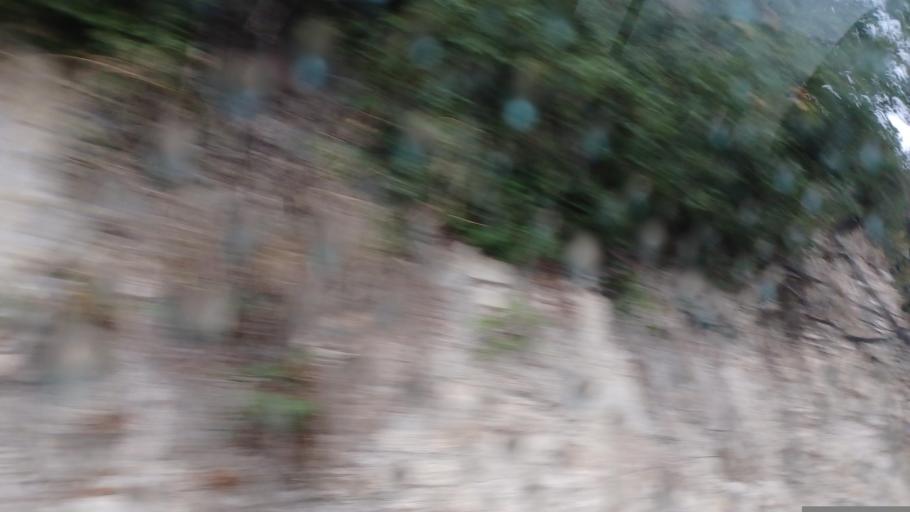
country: CY
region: Pafos
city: Mesogi
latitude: 34.8717
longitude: 32.5405
